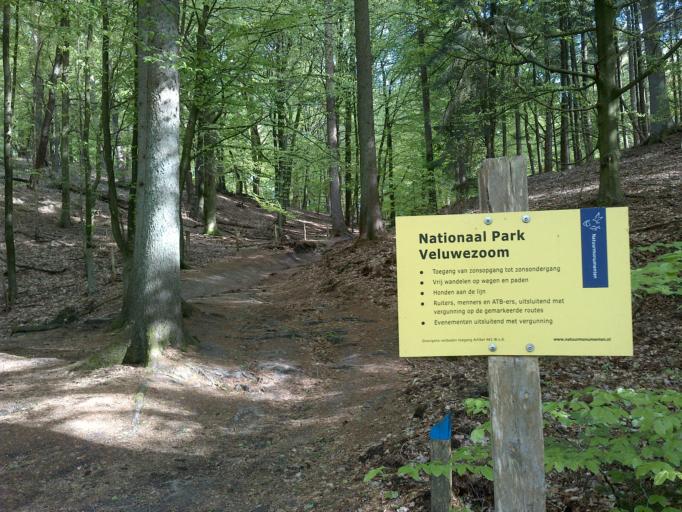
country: NL
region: Gelderland
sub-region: Gemeente Rheden
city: Velp
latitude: 52.0173
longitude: 5.9919
